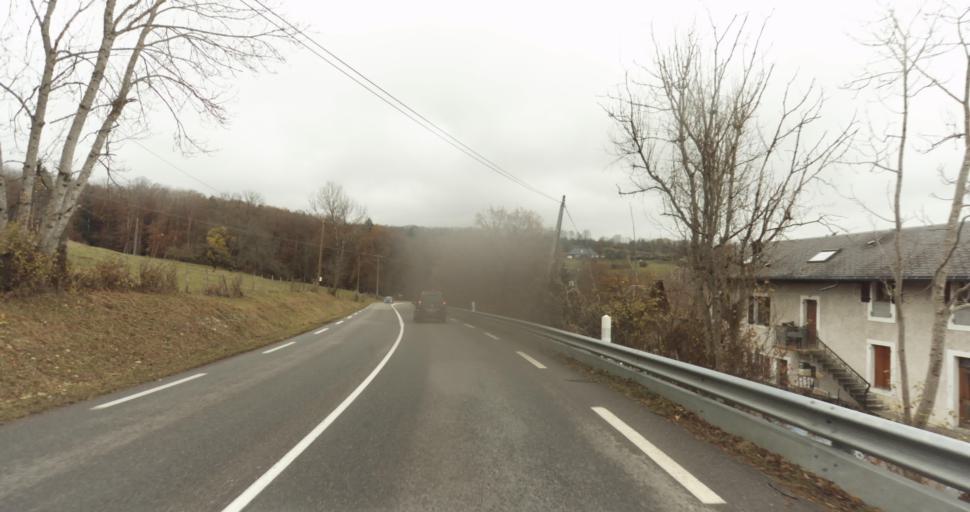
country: FR
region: Rhone-Alpes
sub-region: Departement de la Haute-Savoie
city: Evires
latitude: 46.0352
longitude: 6.2411
